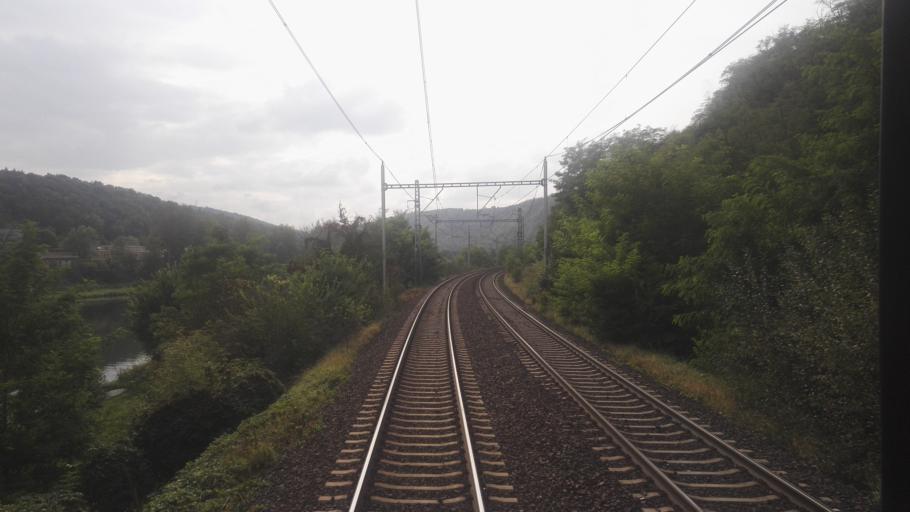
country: CZ
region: Central Bohemia
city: Rez
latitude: 50.1827
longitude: 14.3657
